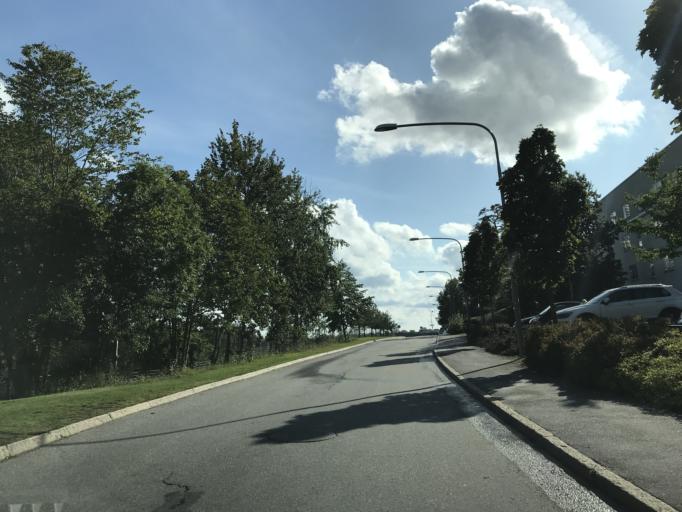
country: SE
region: Stockholm
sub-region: Stockholms Kommun
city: Arsta
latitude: 59.2845
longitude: 18.0179
